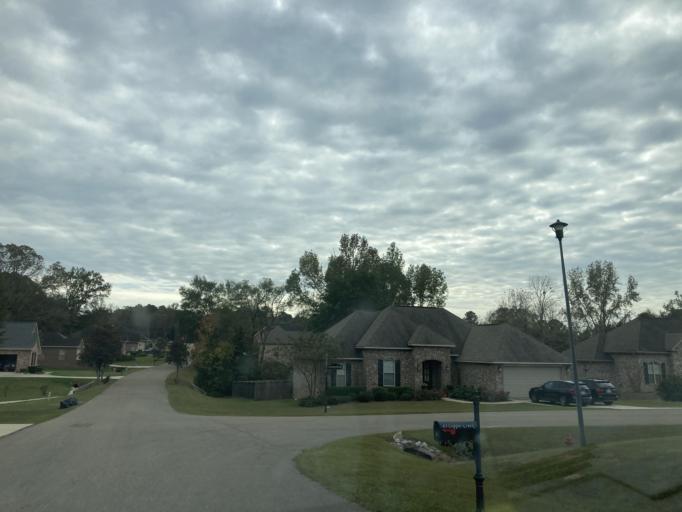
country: US
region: Mississippi
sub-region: Lamar County
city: West Hattiesburg
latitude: 31.2910
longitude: -89.4421
